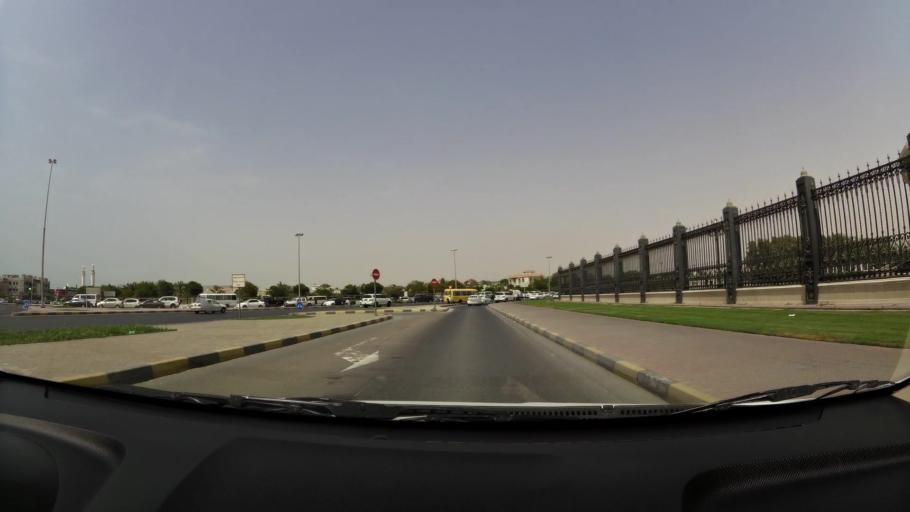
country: AE
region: Ash Shariqah
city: Sharjah
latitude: 25.3558
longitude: 55.4045
